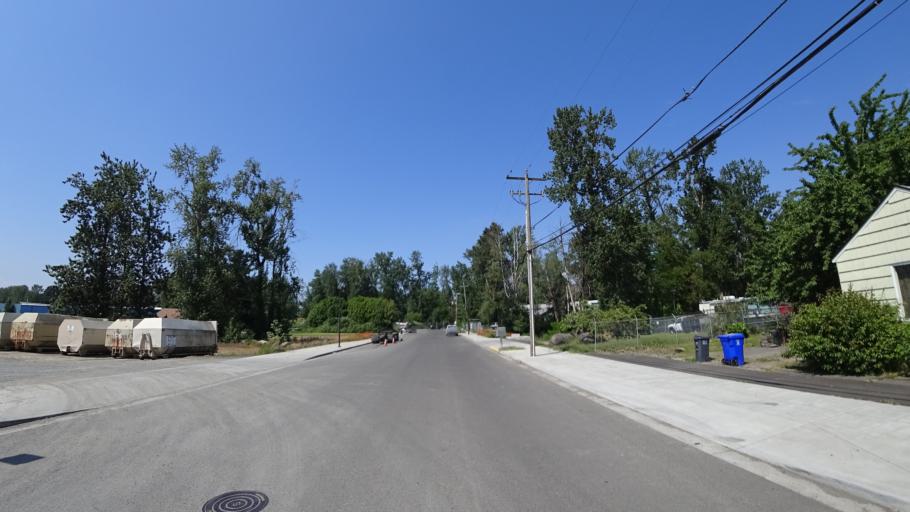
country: US
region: Oregon
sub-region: Multnomah County
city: Lents
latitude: 45.5616
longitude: -122.5474
